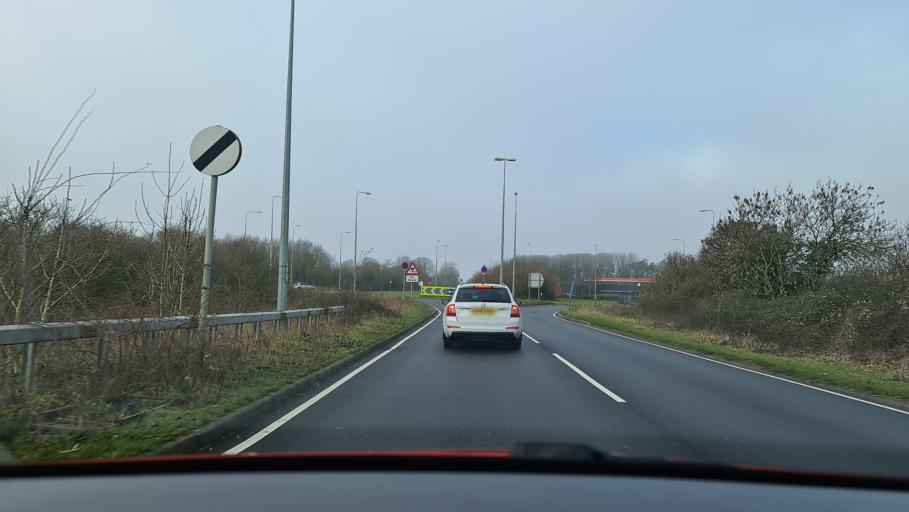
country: GB
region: England
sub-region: Oxfordshire
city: Bicester
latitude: 51.9572
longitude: -1.2008
